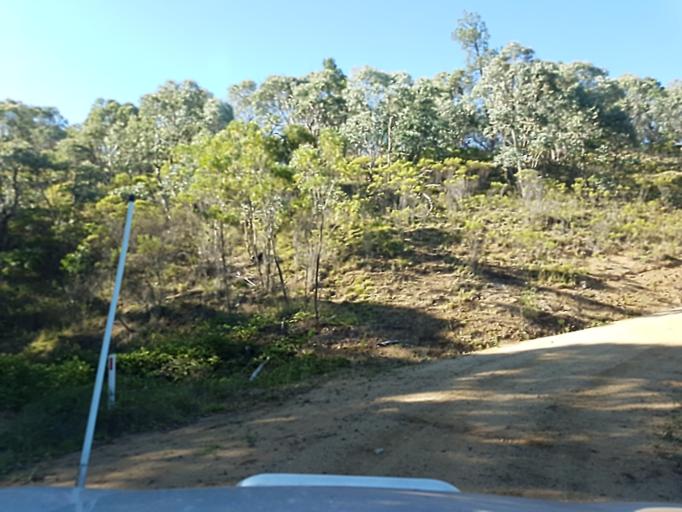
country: AU
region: New South Wales
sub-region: Snowy River
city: Jindabyne
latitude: -36.9359
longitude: 148.3400
